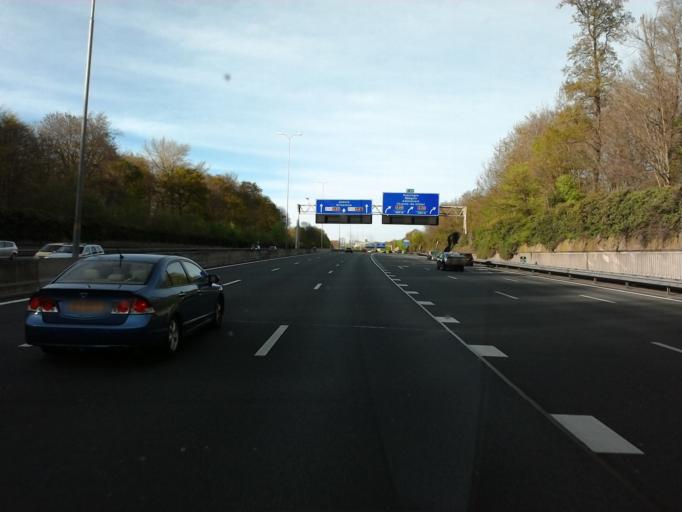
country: NL
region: Utrecht
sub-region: Gemeente Utrecht
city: Lunetten
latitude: 52.0723
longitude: 5.1523
